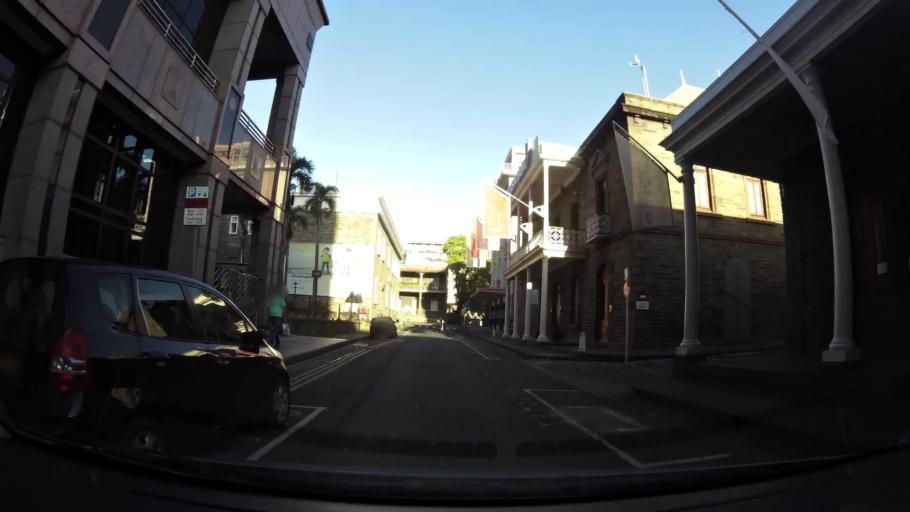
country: MU
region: Port Louis
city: Port Louis
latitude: -20.1624
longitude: 57.5019
